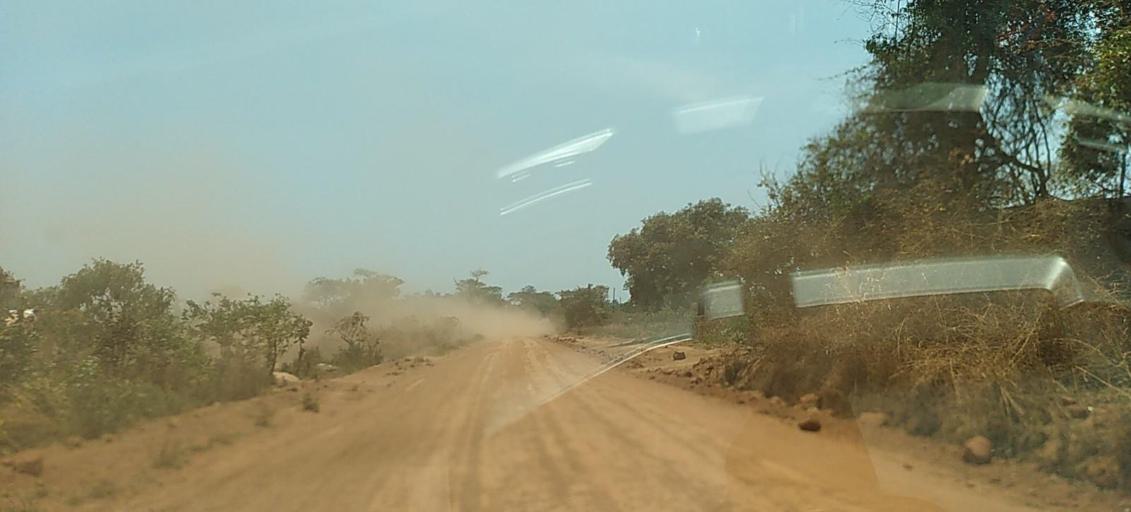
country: CD
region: Katanga
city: Kipushi
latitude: -11.8643
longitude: 27.1137
